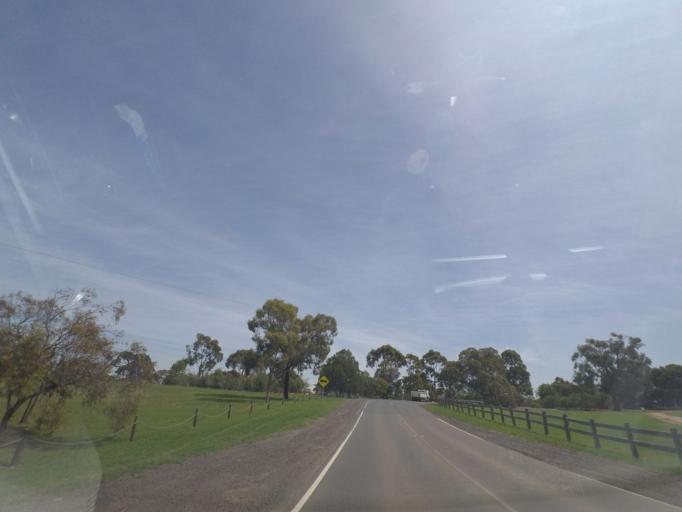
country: AU
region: Victoria
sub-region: Brimbank
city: Keilor Park
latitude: -37.7138
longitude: 144.8572
